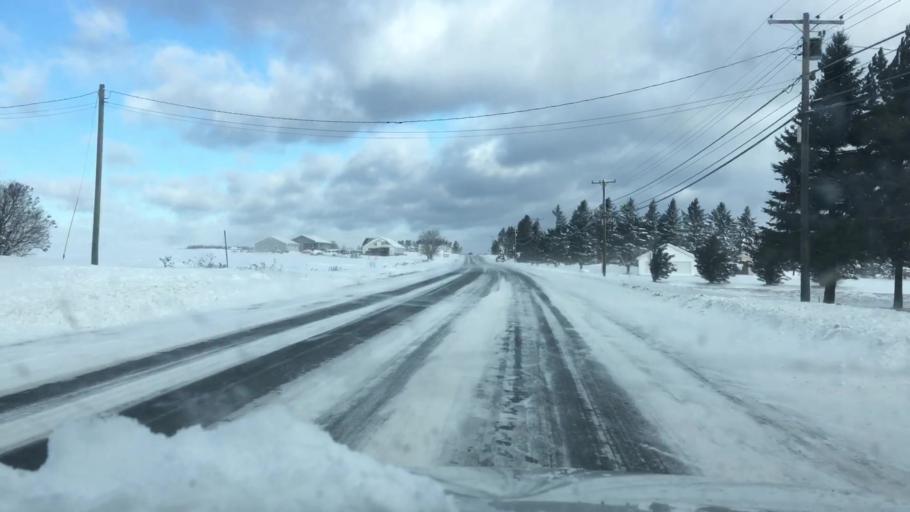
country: US
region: Maine
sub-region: Aroostook County
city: Caribou
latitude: 46.9064
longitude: -68.0160
